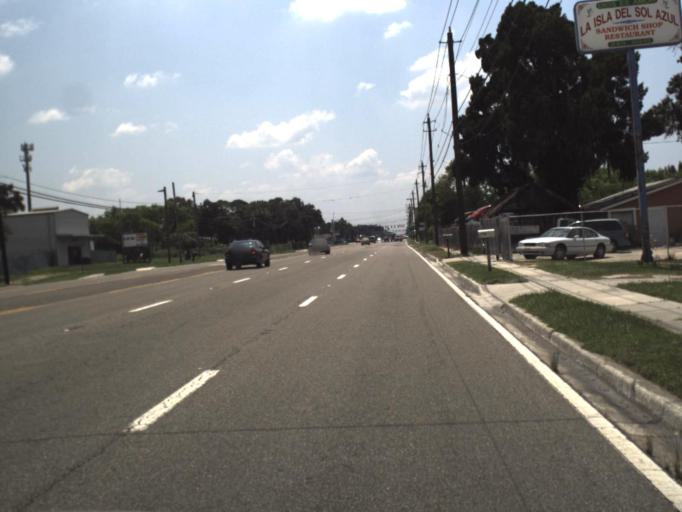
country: US
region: Florida
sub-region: Hillsborough County
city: Palm River-Clair Mel
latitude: 27.9273
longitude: -82.4020
